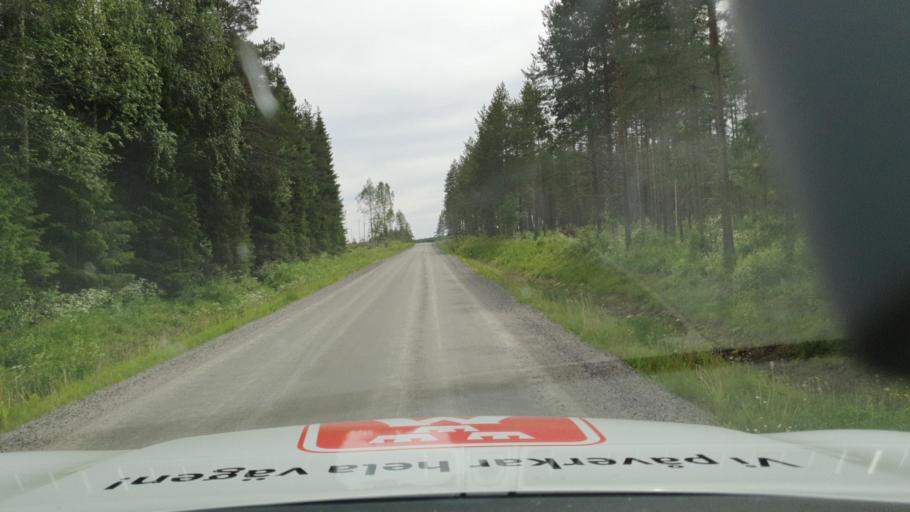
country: SE
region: Vaesterbotten
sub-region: Skelleftea Kommun
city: Burea
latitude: 64.4196
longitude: 21.0085
